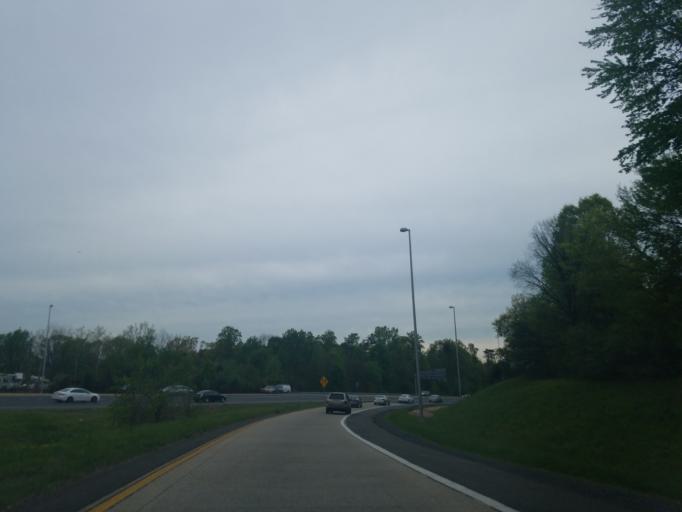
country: US
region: Virginia
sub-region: Fairfax County
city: Centreville
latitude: 38.8486
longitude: -77.4321
